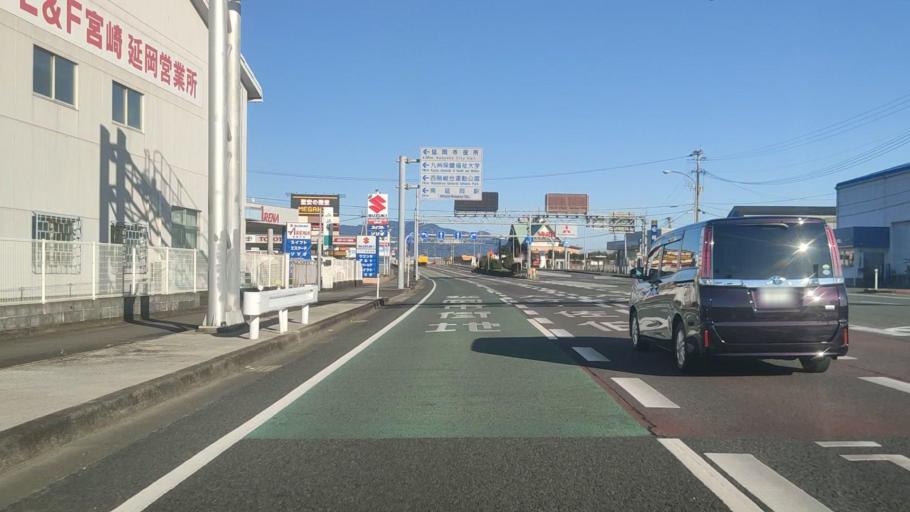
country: JP
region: Miyazaki
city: Nobeoka
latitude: 32.5427
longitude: 131.6783
